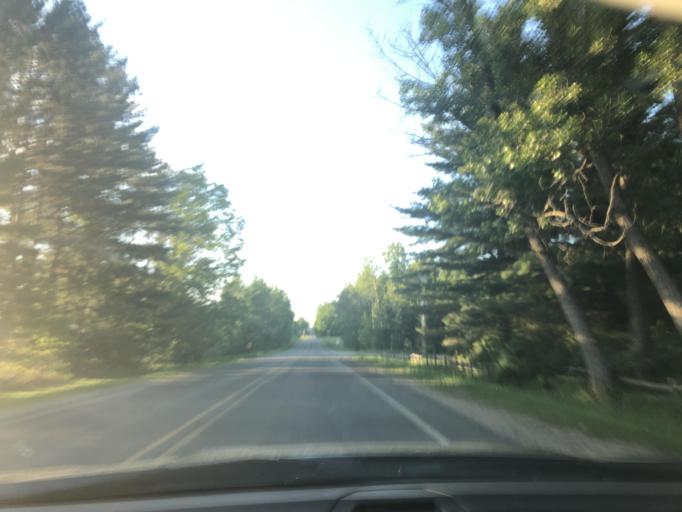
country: US
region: Michigan
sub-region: Missaukee County
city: Lake City
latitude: 44.4510
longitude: -85.0747
